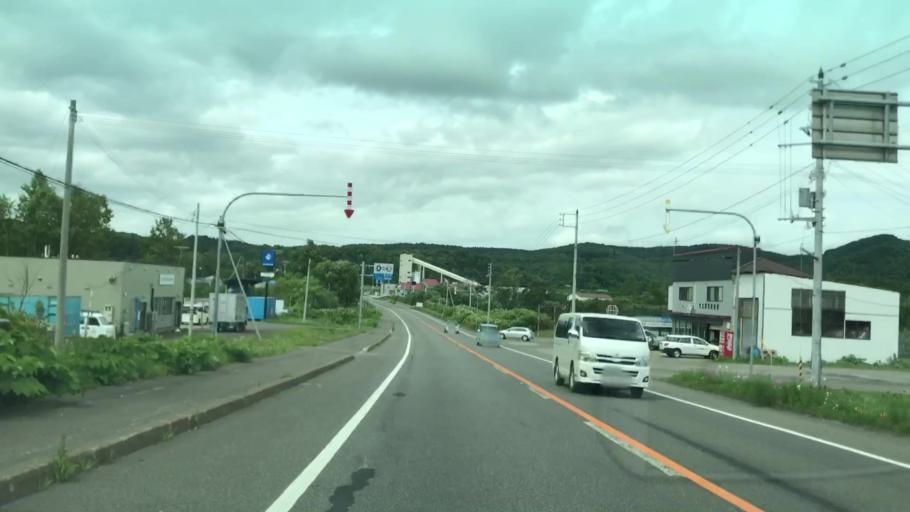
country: JP
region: Hokkaido
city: Niseko Town
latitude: 42.9179
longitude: 140.7462
